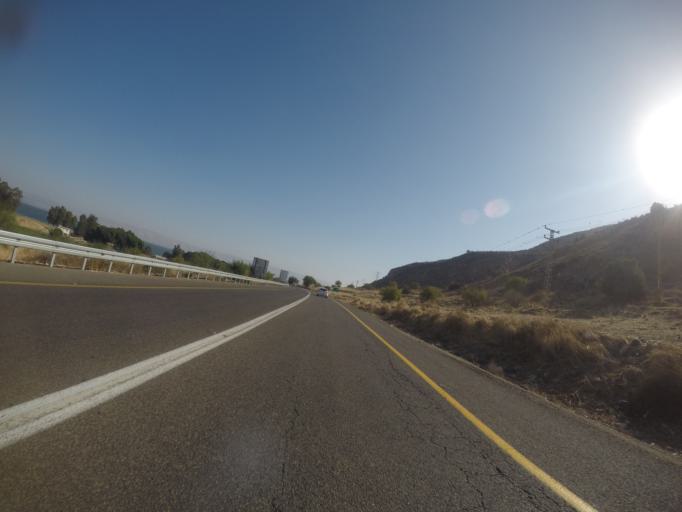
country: IL
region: Northern District
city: Tiberias
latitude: 32.8253
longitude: 35.5130
